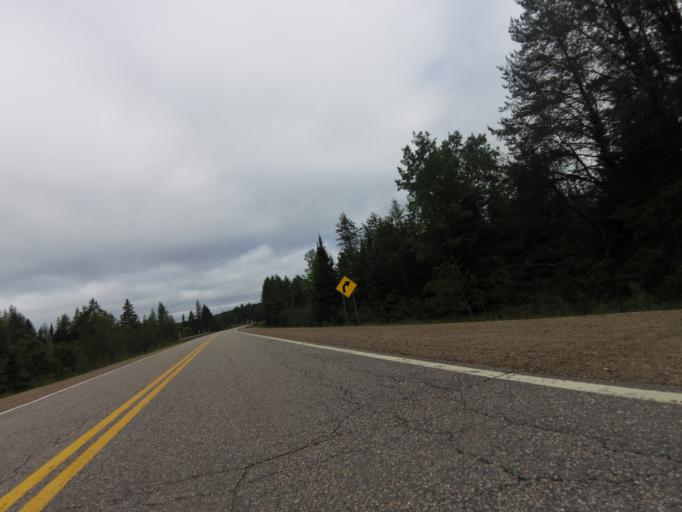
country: CA
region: Quebec
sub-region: Outaouais
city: Shawville
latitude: 45.9071
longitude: -76.3048
